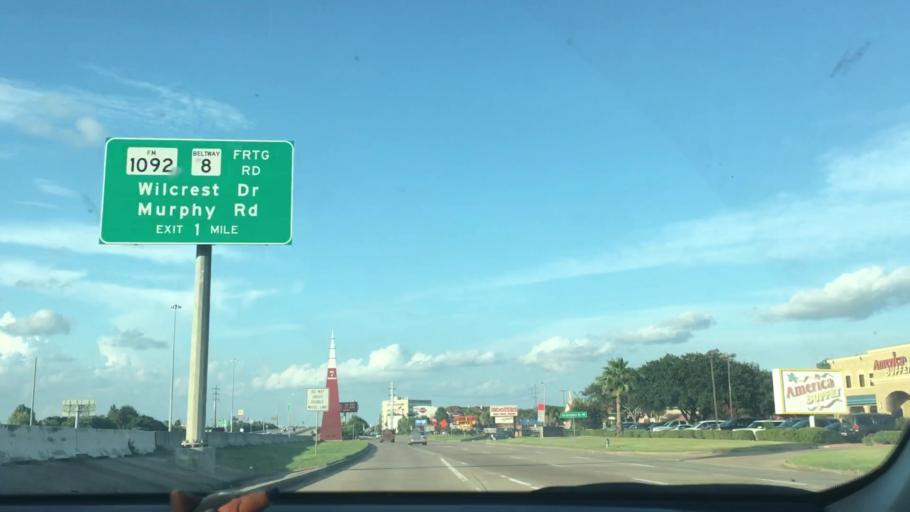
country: US
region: Texas
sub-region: Fort Bend County
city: Meadows Place
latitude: 29.6333
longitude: -95.5873
